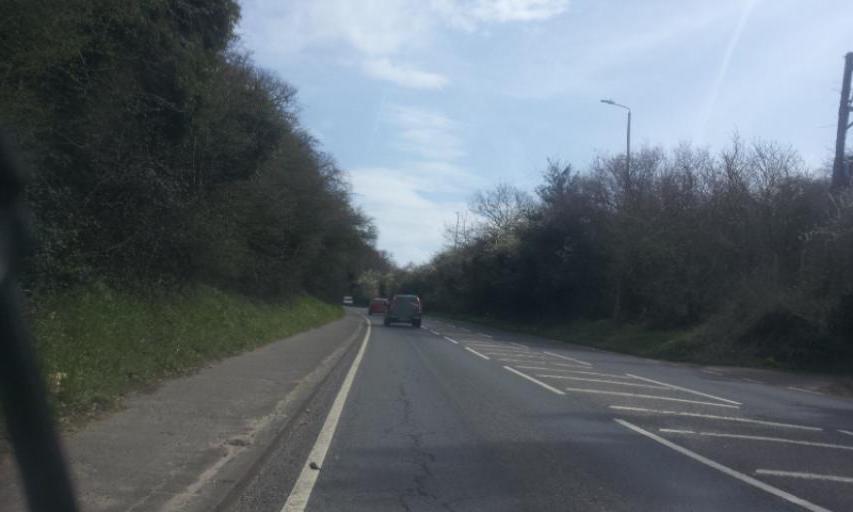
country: GB
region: England
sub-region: Kent
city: Newington
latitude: 51.3501
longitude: 0.6773
